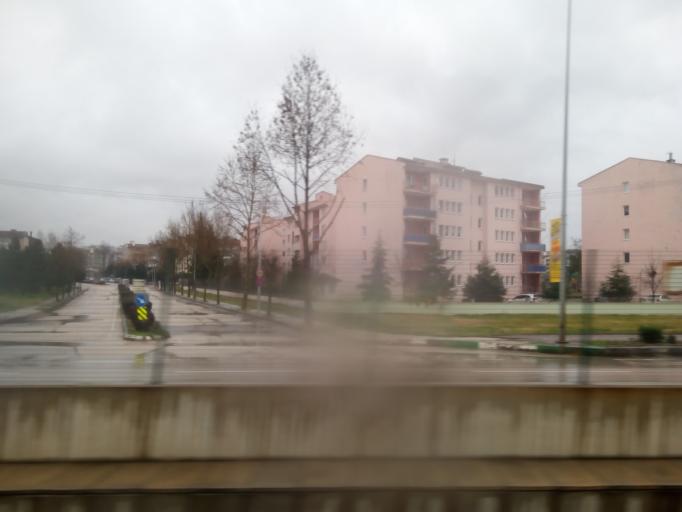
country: TR
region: Bursa
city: Niluefer
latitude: 40.2451
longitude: 28.9650
